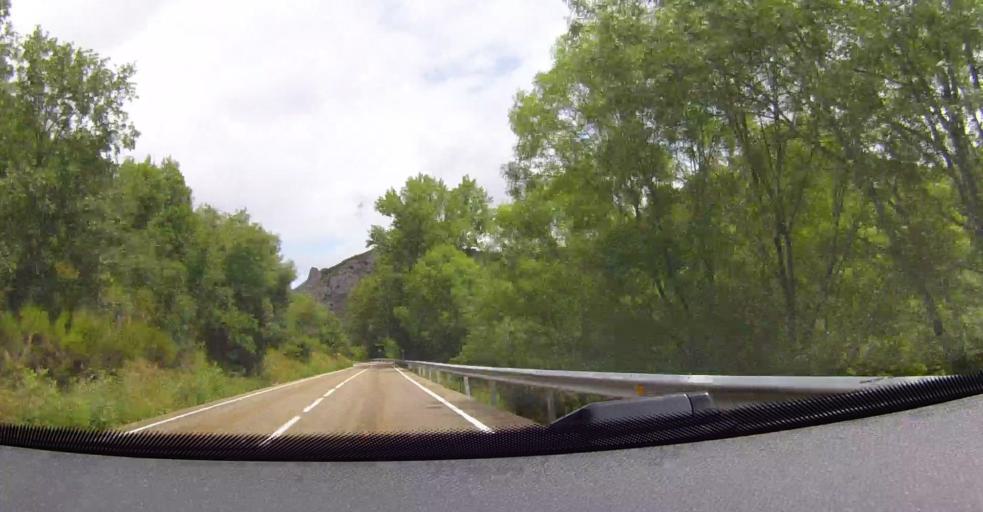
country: ES
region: Castille and Leon
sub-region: Provincia de Leon
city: Bonar
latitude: 42.9006
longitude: -5.3136
